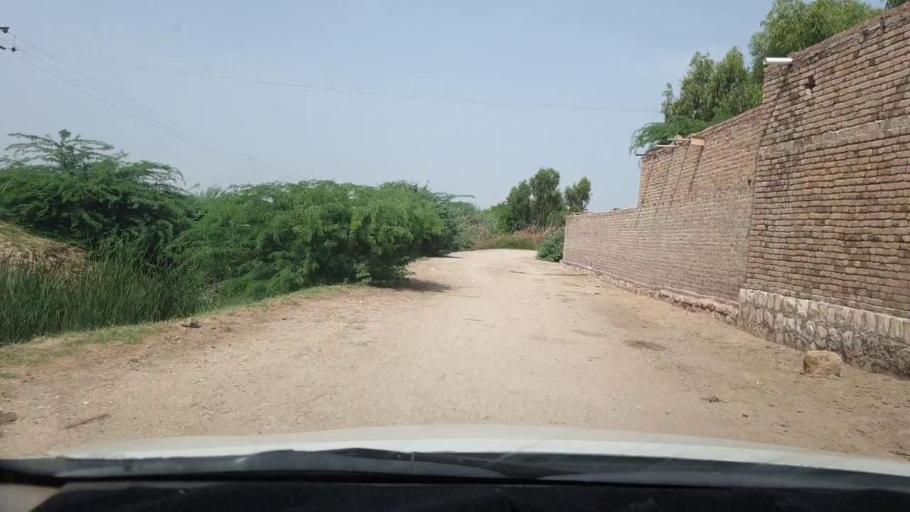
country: PK
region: Sindh
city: Rohri
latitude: 27.5959
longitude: 68.9817
